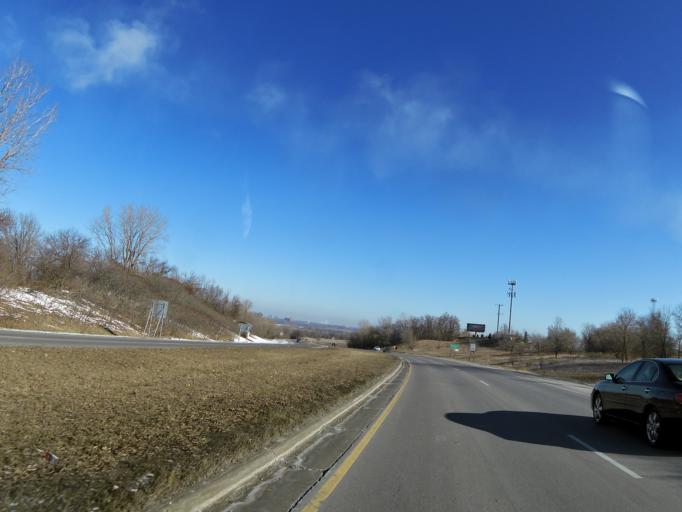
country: US
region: Minnesota
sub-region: Dakota County
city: Eagan
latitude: 44.8058
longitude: -93.2281
